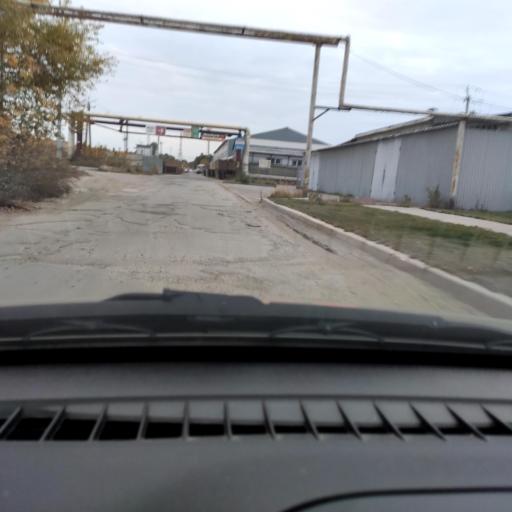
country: RU
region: Samara
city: Tol'yatti
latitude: 53.5760
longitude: 49.2838
